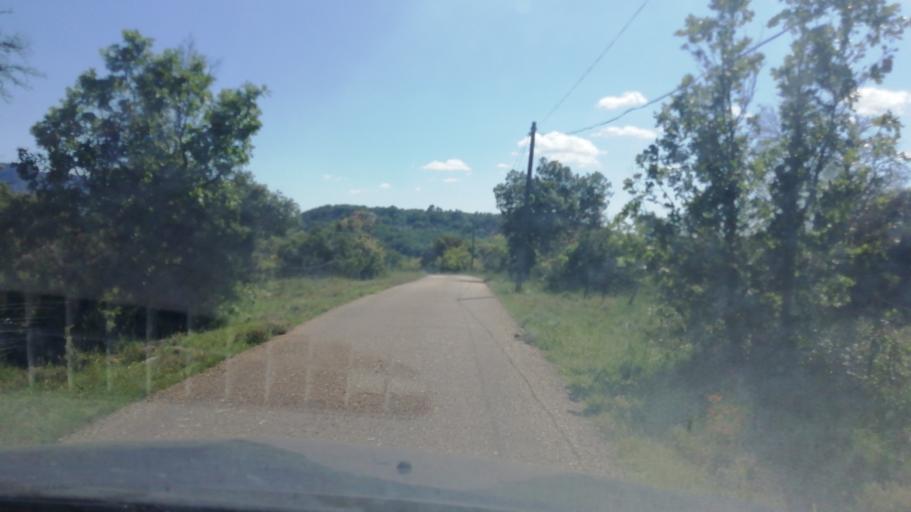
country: FR
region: Languedoc-Roussillon
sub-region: Departement de l'Herault
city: Saint-Mathieu-de-Treviers
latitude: 43.8261
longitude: 3.8130
